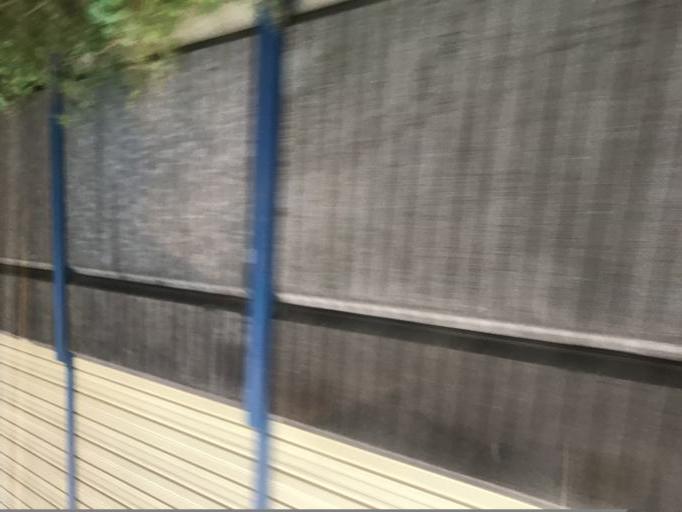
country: VA
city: Vatican City
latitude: 41.8580
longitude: 12.4582
